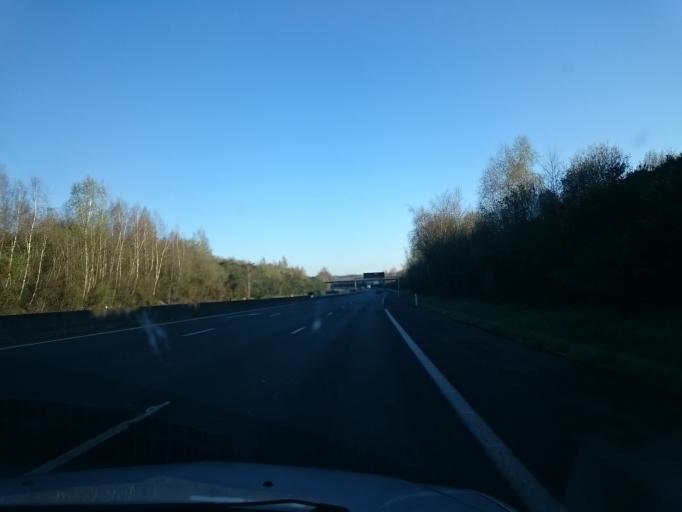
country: FR
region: Brittany
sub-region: Departement d'Ille-et-Vilaine
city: Cesson-Sevigne
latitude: 48.1275
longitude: -1.5743
